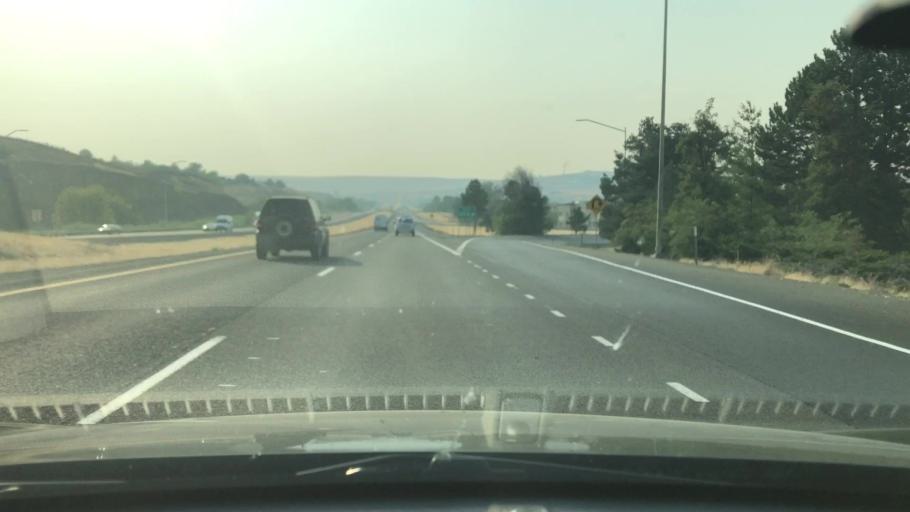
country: US
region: Oregon
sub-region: Umatilla County
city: Pendleton
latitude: 45.6634
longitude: -118.8071
